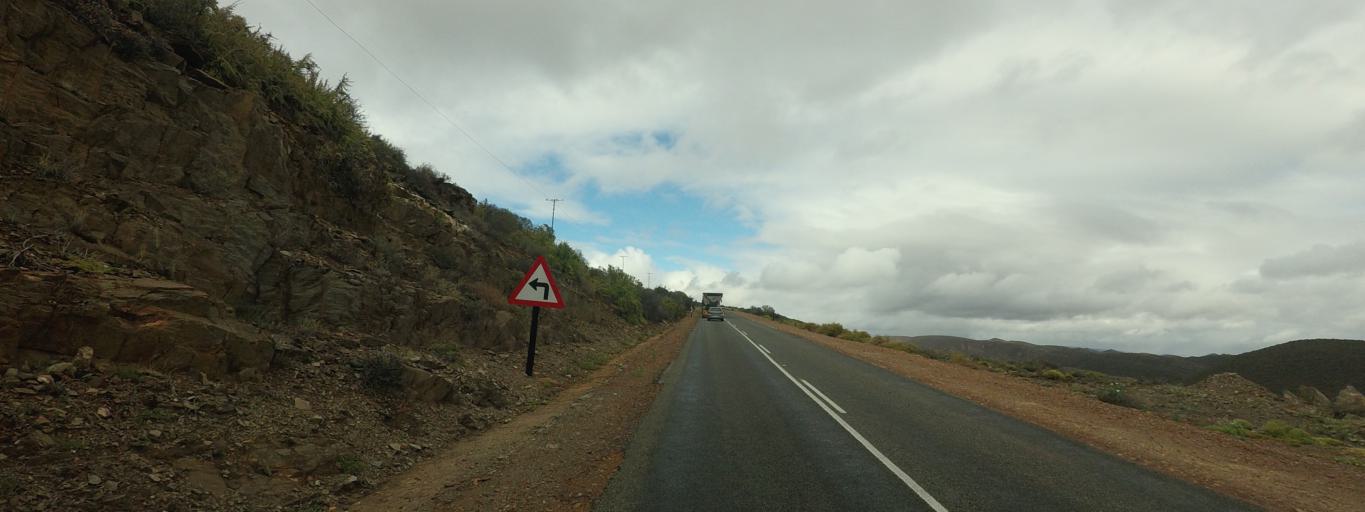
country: ZA
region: Western Cape
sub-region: Eden District Municipality
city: Oudtshoorn
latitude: -33.6871
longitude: 22.2711
